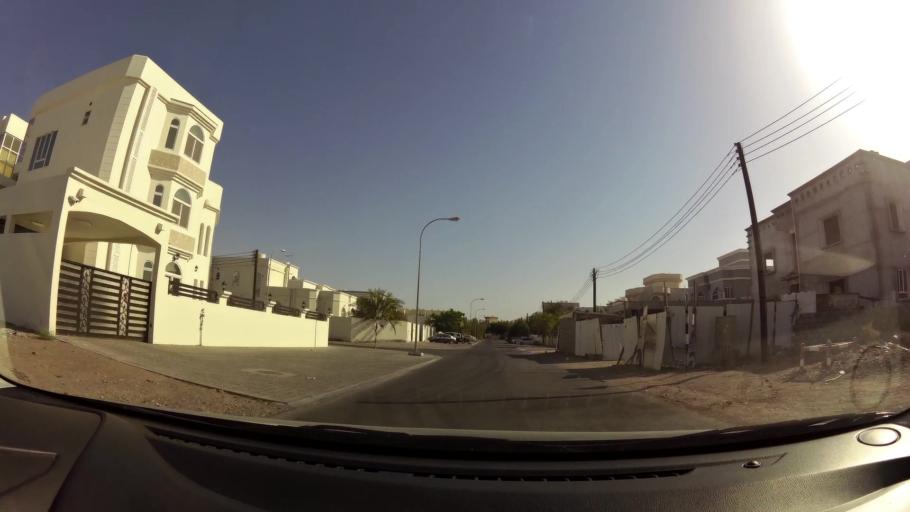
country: OM
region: Muhafazat Masqat
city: As Sib al Jadidah
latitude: 23.6172
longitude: 58.2111
